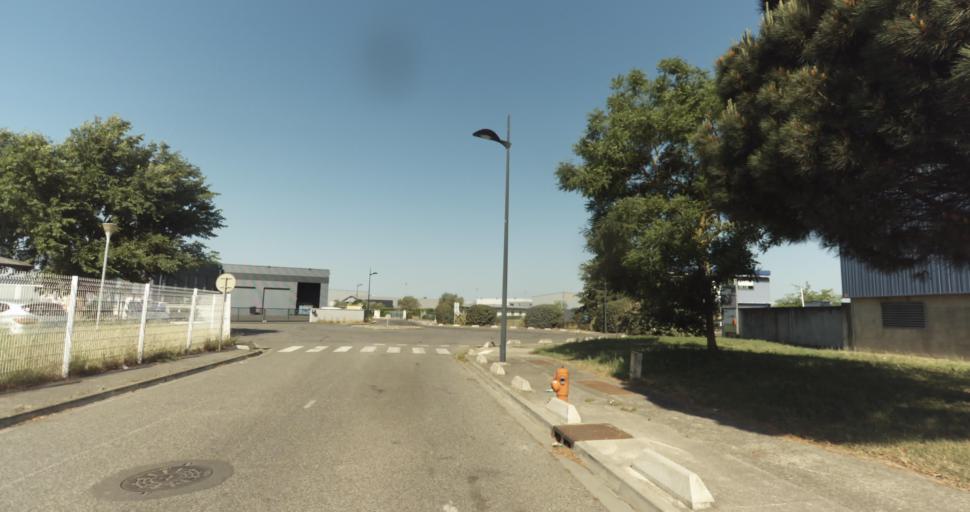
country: FR
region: Midi-Pyrenees
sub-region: Departement de la Haute-Garonne
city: Tournefeuille
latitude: 43.5960
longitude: 1.2964
